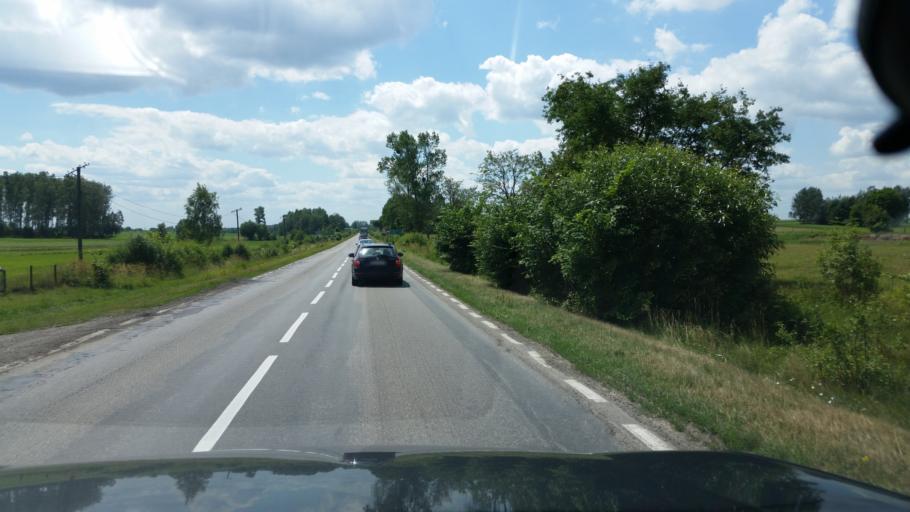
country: PL
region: Podlasie
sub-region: Powiat lomzynski
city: Sniadowo
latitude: 53.0584
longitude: 21.9998
